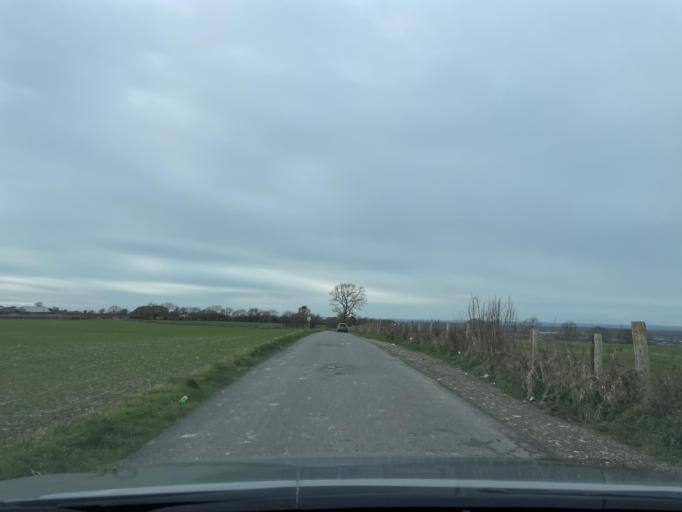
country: GB
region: England
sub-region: Borough of Swindon
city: Wroughton
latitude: 51.5134
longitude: -1.8156
